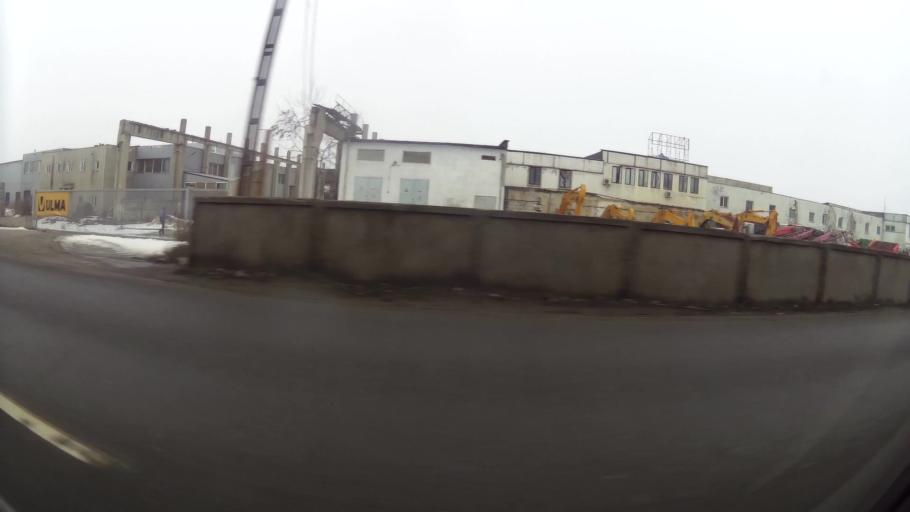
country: RO
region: Ilfov
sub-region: Comuna Bragadiru
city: Bragadiru
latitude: 44.3887
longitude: 25.9866
